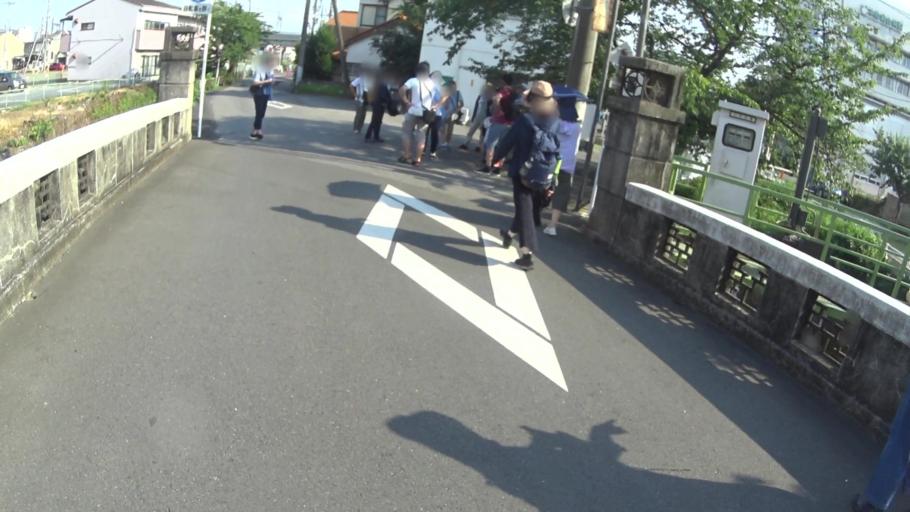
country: JP
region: Gunma
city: Ota
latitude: 36.2958
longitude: 139.3703
